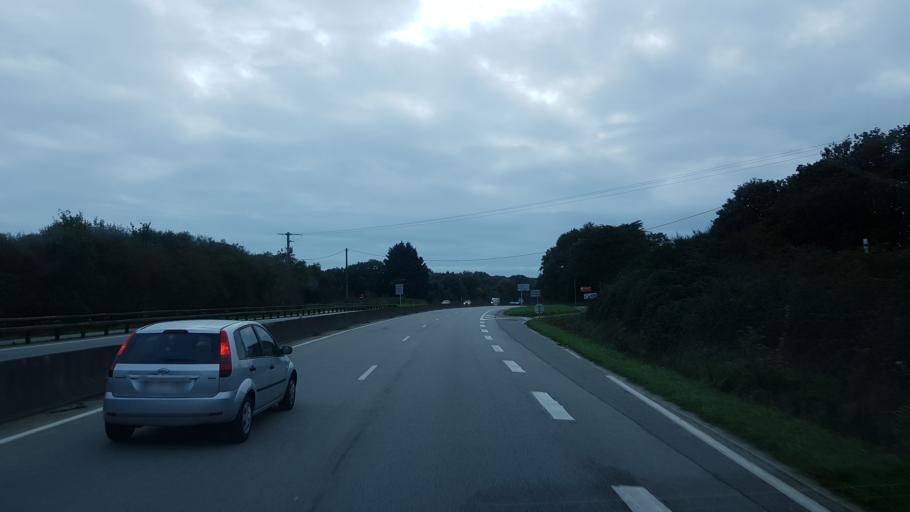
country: FR
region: Brittany
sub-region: Departement du Morbihan
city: Sarzeau
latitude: 47.5451
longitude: -2.7219
